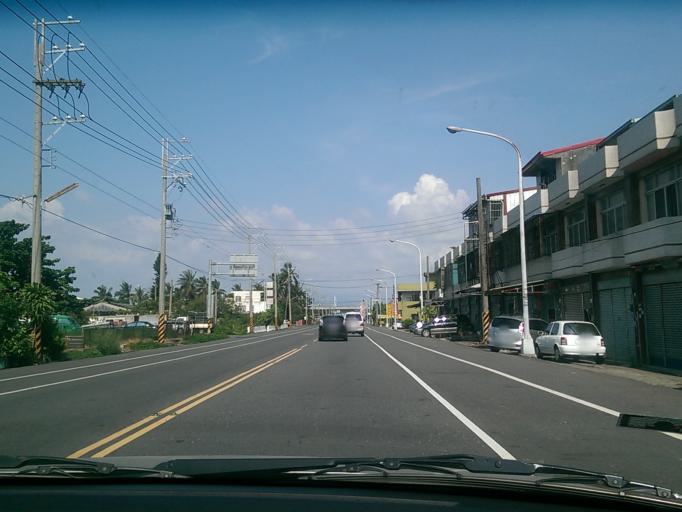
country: TW
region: Taiwan
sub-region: Chiayi
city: Taibao
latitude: 23.5602
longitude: 120.3252
